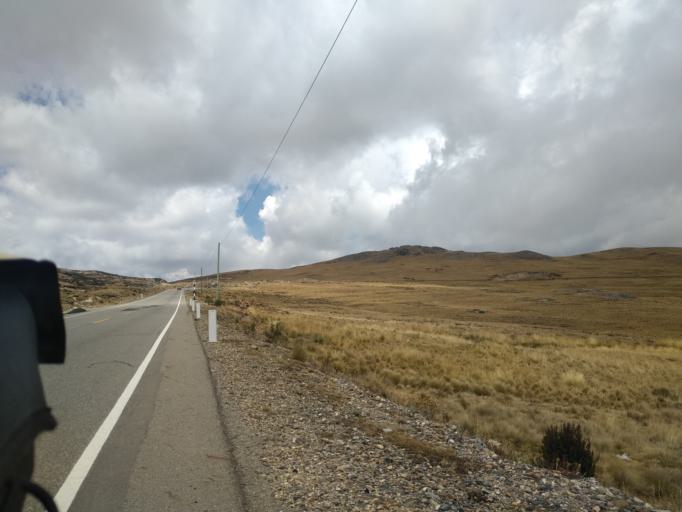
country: PE
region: La Libertad
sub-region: Provincia de Santiago de Chuco
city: Quiruvilca
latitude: -7.9467
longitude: -78.1905
